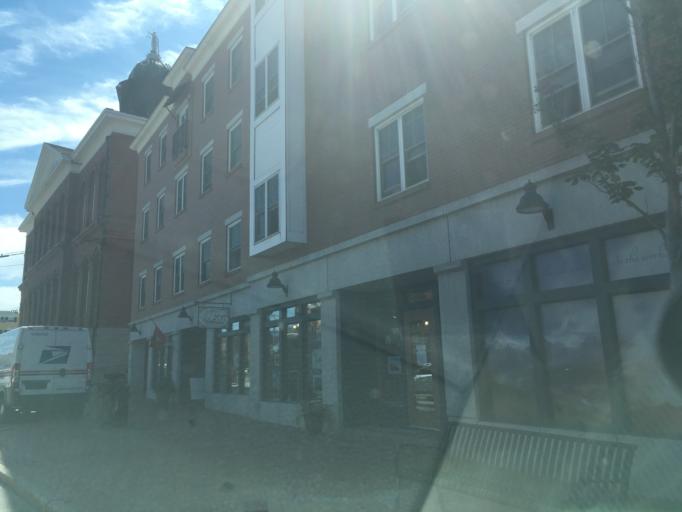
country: US
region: New Hampshire
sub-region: Rockingham County
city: Exeter
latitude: 42.9815
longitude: -70.9477
